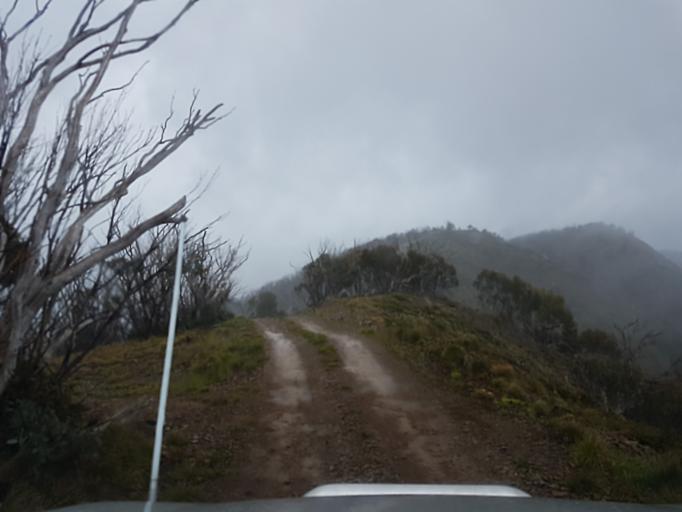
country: AU
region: Victoria
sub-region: Alpine
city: Mount Beauty
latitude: -37.0927
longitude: 147.0679
